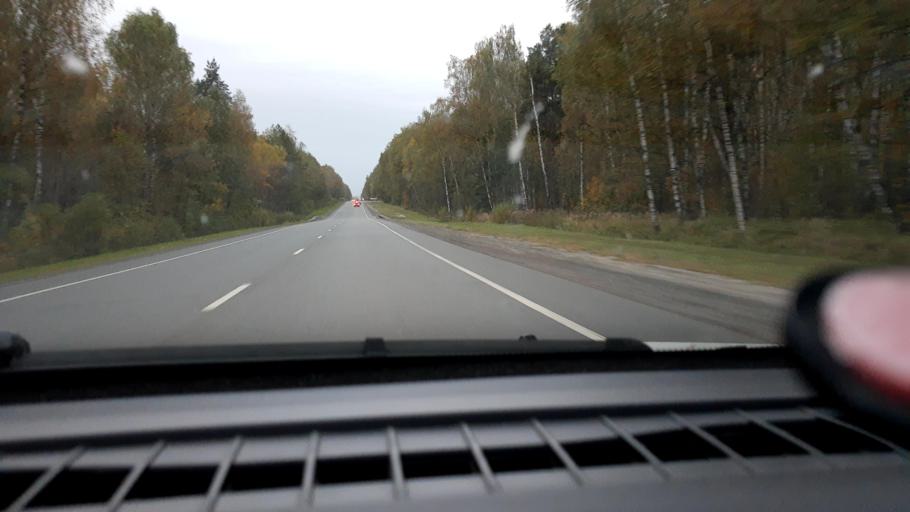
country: RU
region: Vladimir
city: Orgtrud
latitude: 56.2099
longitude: 40.6368
